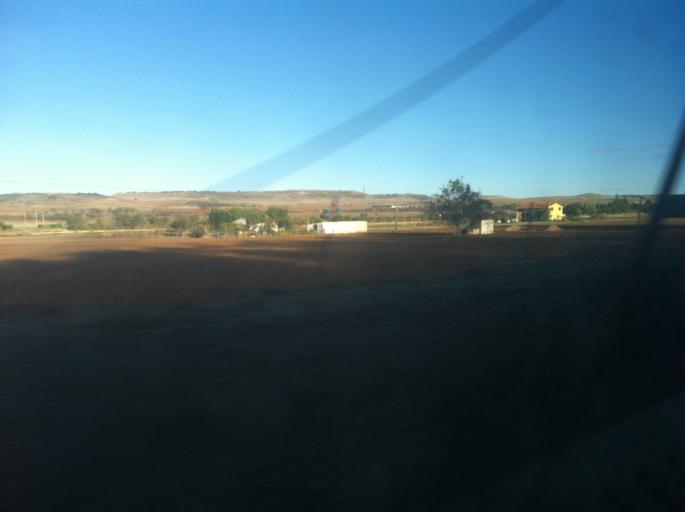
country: ES
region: Castille and Leon
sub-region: Provincia de Palencia
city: Duenas
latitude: 41.8420
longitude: -4.5591
